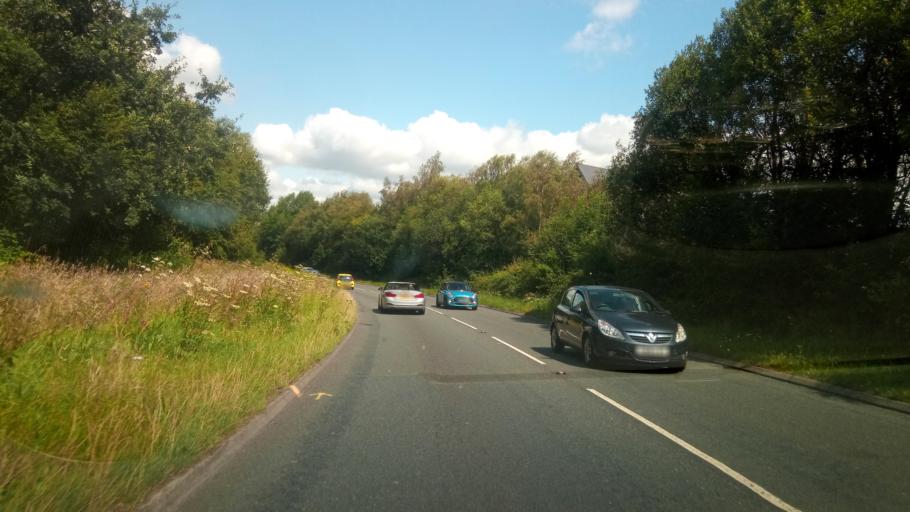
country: GB
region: Wales
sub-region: Caerphilly County Borough
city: Caerphilly
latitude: 51.5717
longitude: -3.2463
